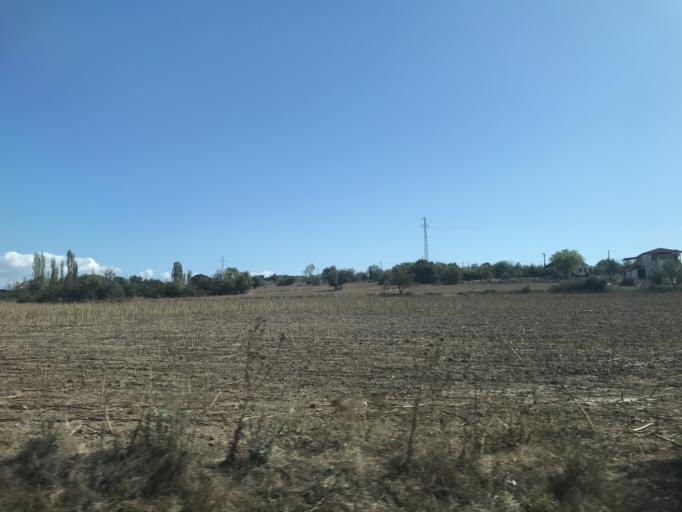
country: TR
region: Kirklareli
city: Kirklareli
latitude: 41.7779
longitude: 27.2278
